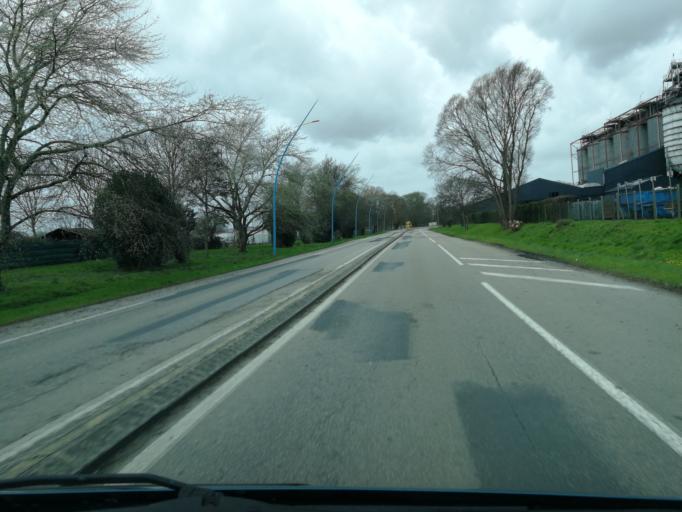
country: FR
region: Haute-Normandie
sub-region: Departement de l'Eure
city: Quillebeuf-sur-Seine
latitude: 49.4749
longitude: 0.5347
